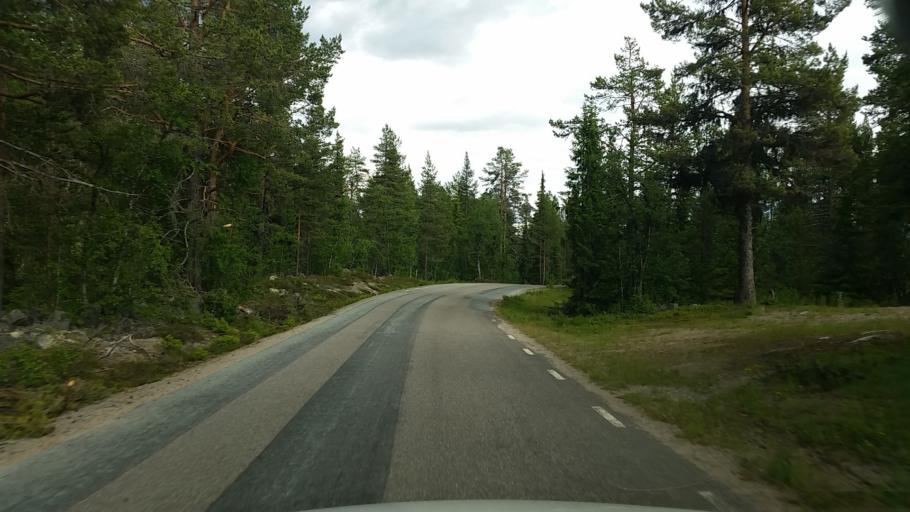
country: SE
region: Jaemtland
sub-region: Harjedalens Kommun
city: Sveg
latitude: 62.1269
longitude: 13.1728
